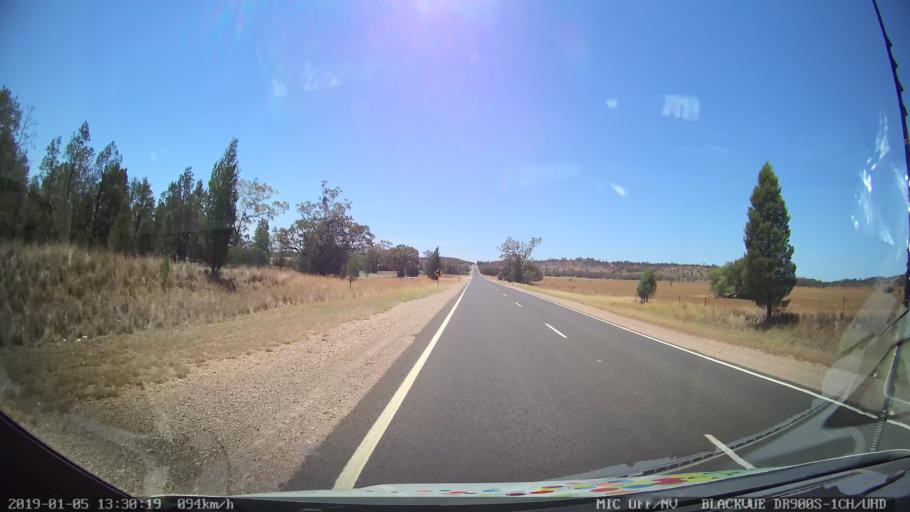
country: AU
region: New South Wales
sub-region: Gunnedah
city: Gunnedah
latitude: -31.0199
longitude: 150.0690
